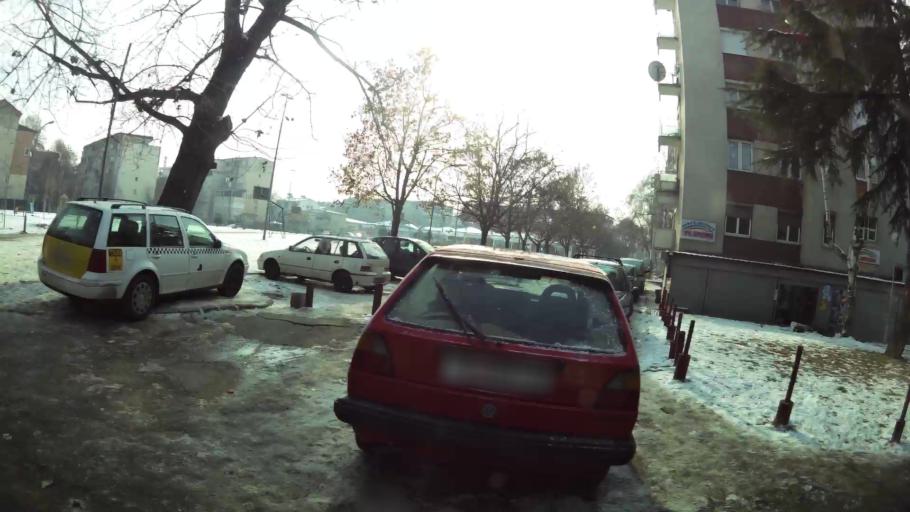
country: MK
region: Cair
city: Cair
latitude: 42.0169
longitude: 21.4327
